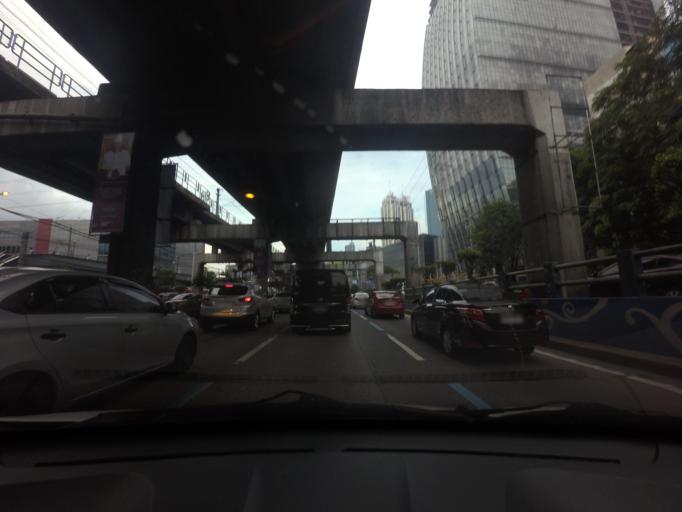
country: PH
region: Metro Manila
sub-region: Pasig
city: Pasig City
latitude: 14.5821
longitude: 121.0563
